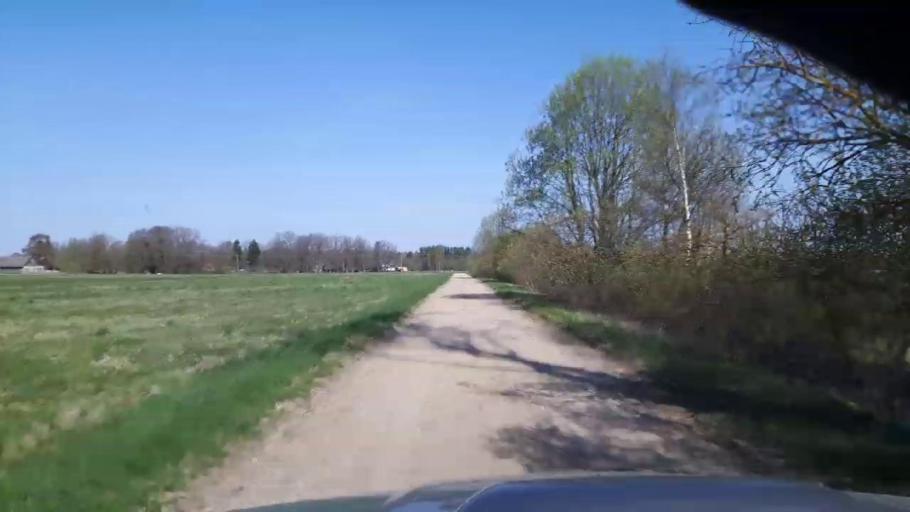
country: EE
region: Paernumaa
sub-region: Tootsi vald
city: Tootsi
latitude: 58.4872
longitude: 24.9279
